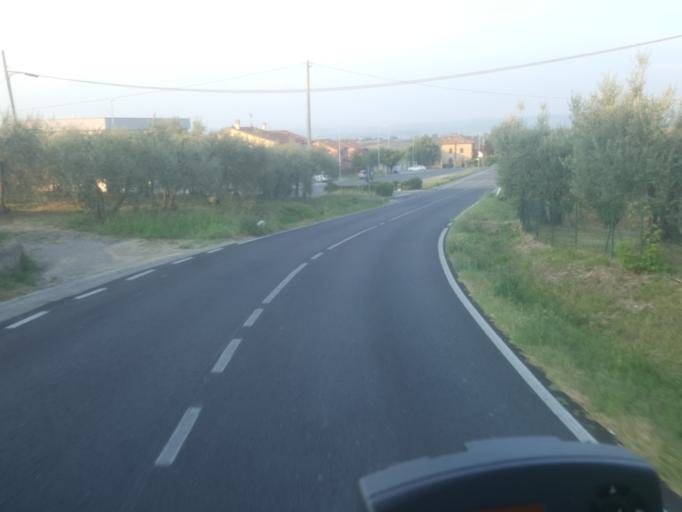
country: IT
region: Tuscany
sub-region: Province of Florence
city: Gambassi Terme
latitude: 43.5421
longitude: 10.9622
